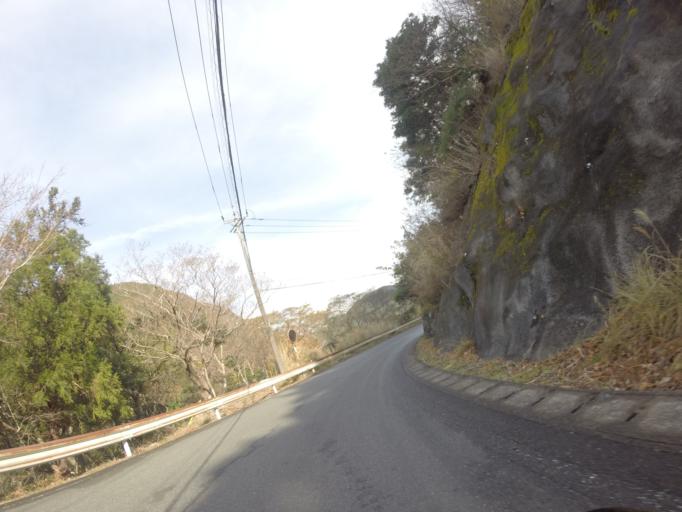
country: JP
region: Shizuoka
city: Heda
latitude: 34.8229
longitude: 138.8352
